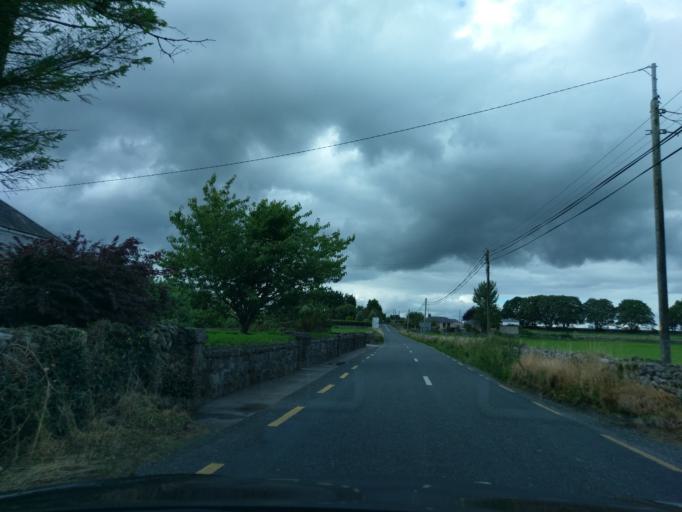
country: IE
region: Connaught
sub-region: County Galway
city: Athenry
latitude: 53.2858
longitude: -8.7442
